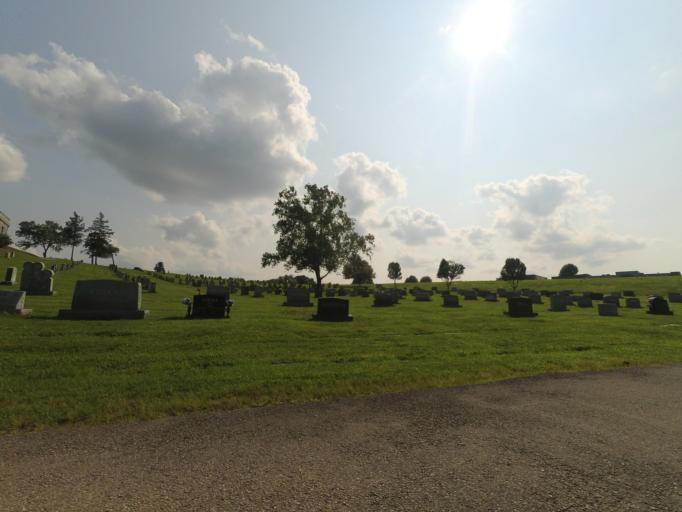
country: US
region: West Virginia
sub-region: Cabell County
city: Huntington
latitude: 38.4055
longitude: -82.3983
